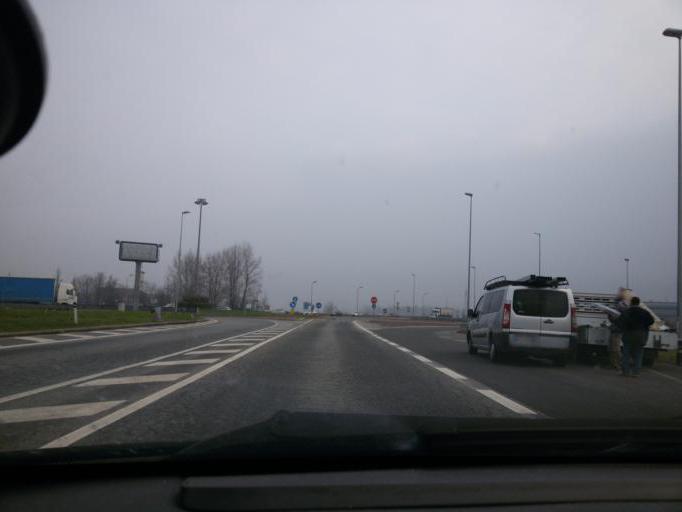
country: IT
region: Piedmont
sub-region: Provincia di Vercelli
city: Asigliano Vercellese
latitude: 45.2963
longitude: 8.3889
